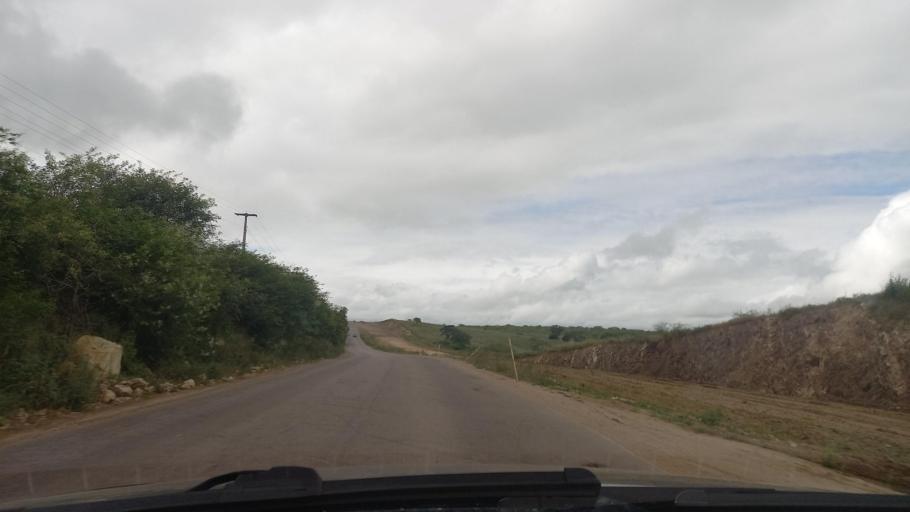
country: BR
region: Alagoas
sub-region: Batalha
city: Batalha
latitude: -9.6414
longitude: -37.1940
